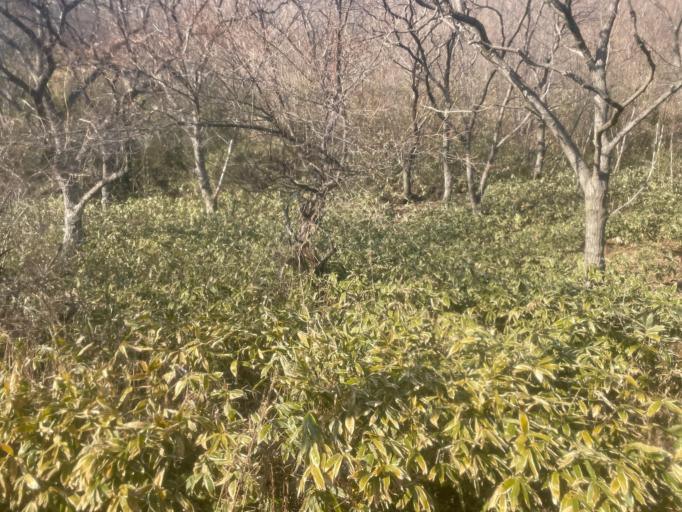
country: JP
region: Gunma
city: Nakanojomachi
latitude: 36.5481
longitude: 138.6012
